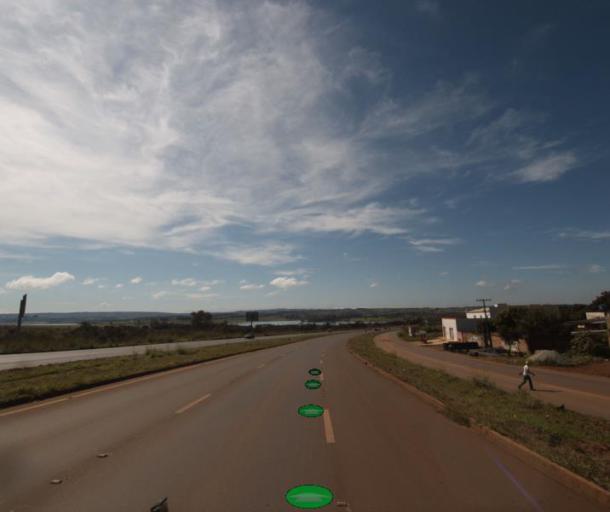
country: BR
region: Federal District
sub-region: Brasilia
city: Brasilia
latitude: -15.7626
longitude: -48.2342
